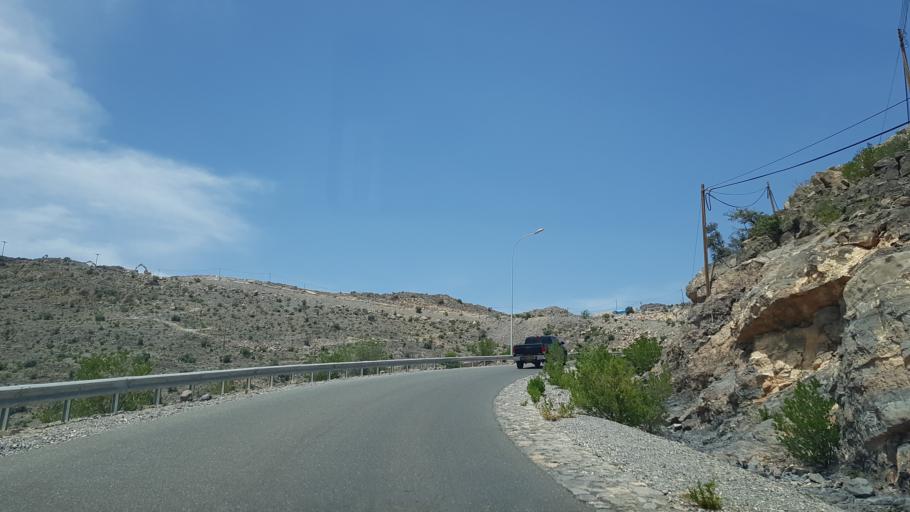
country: OM
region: Muhafazat ad Dakhiliyah
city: Izki
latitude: 23.0911
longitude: 57.6823
